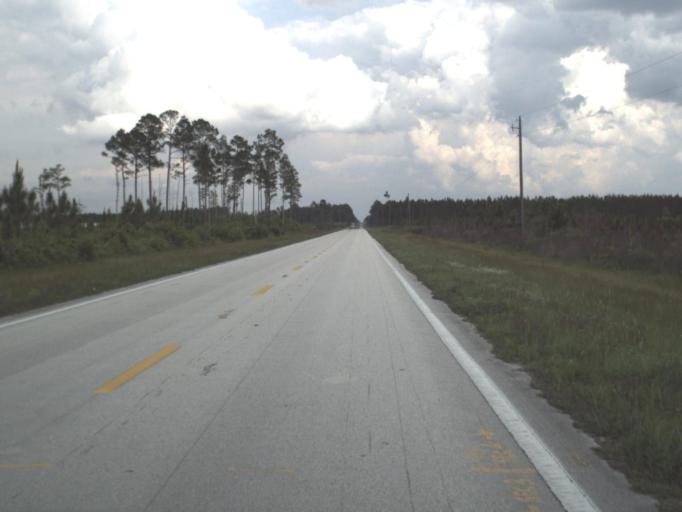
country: US
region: Florida
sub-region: Baker County
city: Macclenny
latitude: 30.5376
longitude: -82.3286
